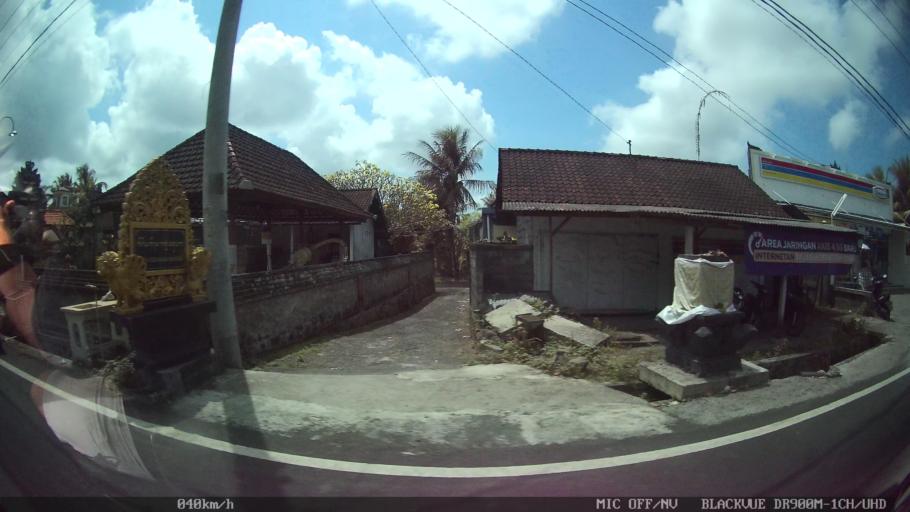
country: ID
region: Bali
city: Banjar Pasekan
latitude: -8.5919
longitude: 115.2970
